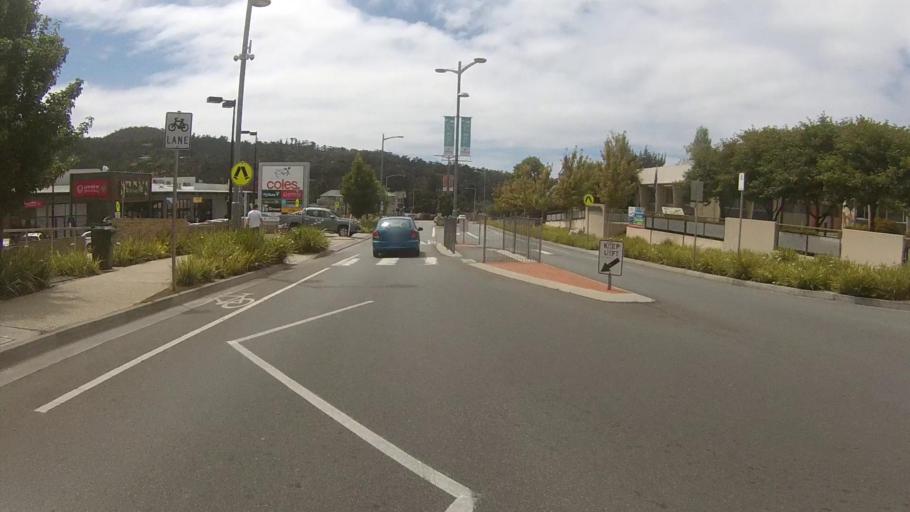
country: AU
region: Tasmania
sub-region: Kingborough
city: Kingston
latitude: -42.9753
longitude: 147.3109
